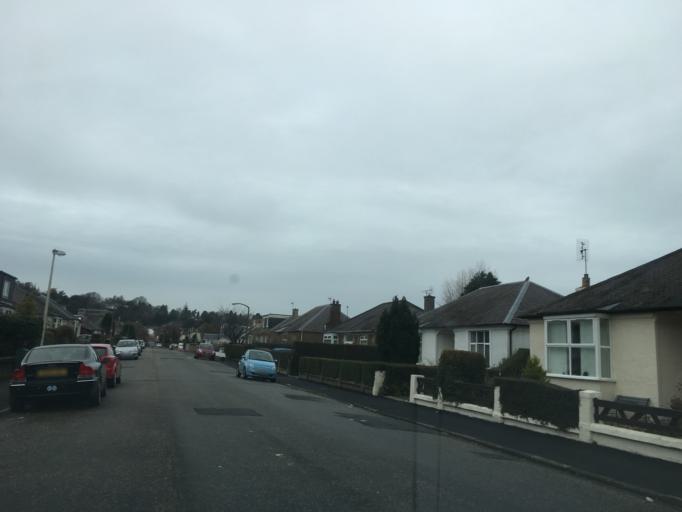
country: GB
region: Scotland
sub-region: Edinburgh
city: Colinton
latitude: 55.9406
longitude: -3.2472
